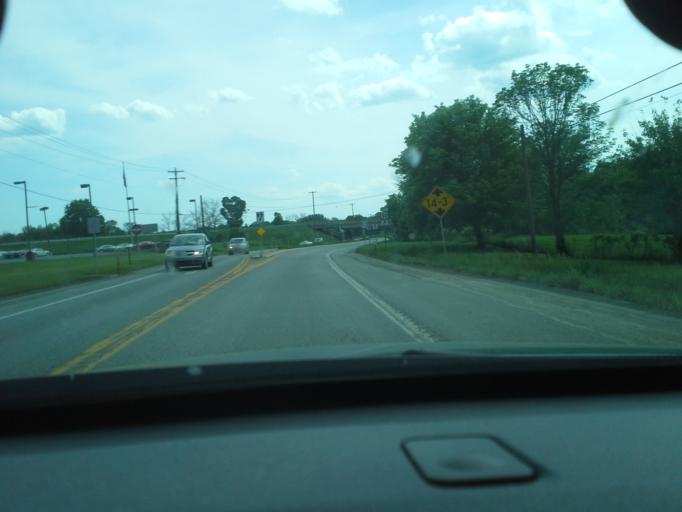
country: US
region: Pennsylvania
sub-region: Fulton County
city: McConnellsburg
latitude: 39.9455
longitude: -77.9918
